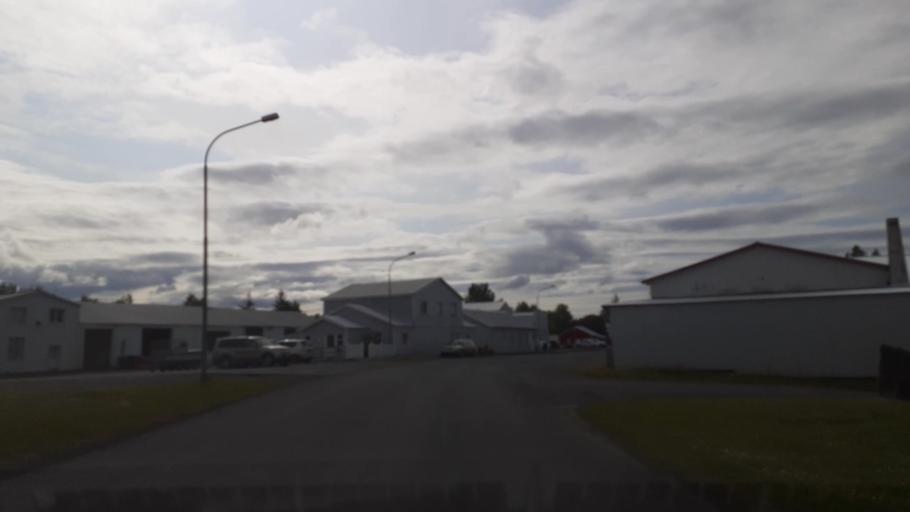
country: IS
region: South
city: Vestmannaeyjar
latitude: 63.8407
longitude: -20.4005
